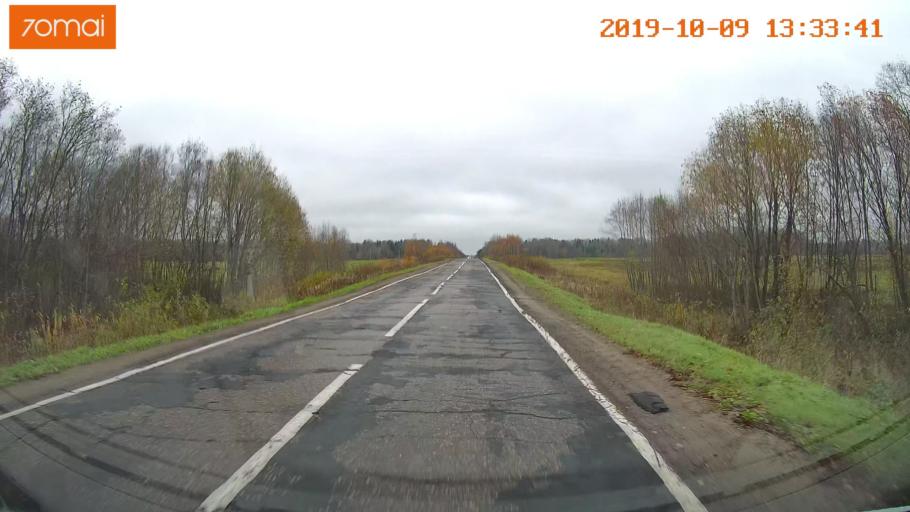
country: RU
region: Jaroslavl
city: Lyubim
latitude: 58.3266
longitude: 41.0507
